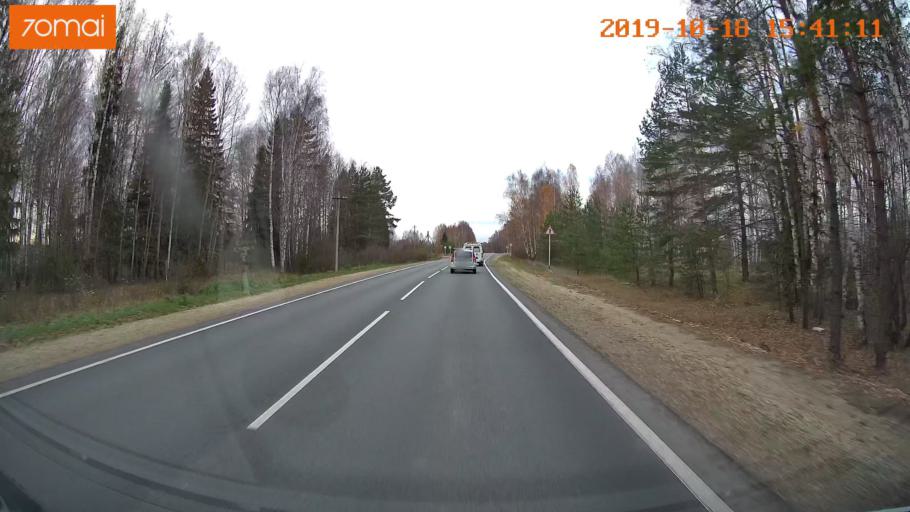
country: RU
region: Vladimir
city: Golovino
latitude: 55.9428
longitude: 40.5861
